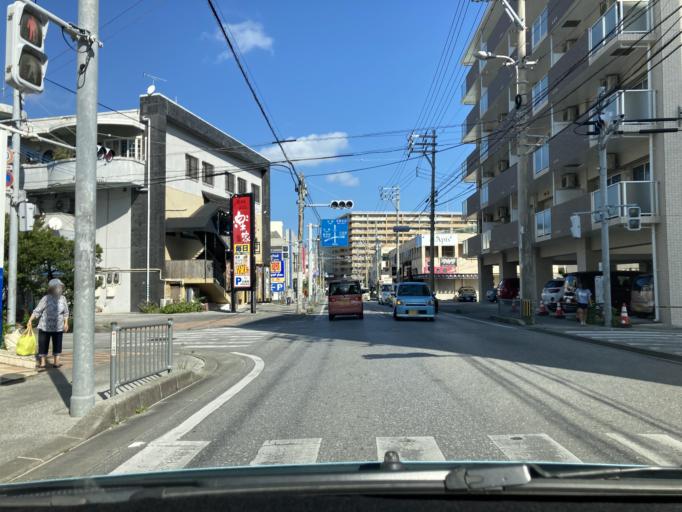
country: JP
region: Okinawa
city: Tomigusuku
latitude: 26.1902
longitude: 127.6603
